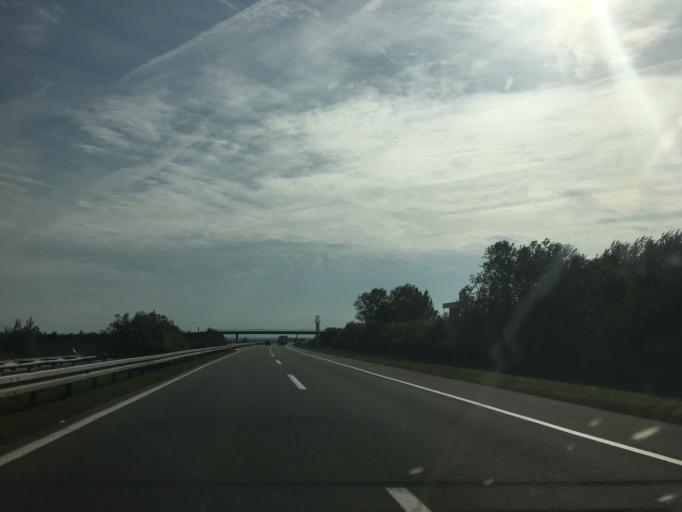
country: RS
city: Novi Banovci
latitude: 44.9191
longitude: 20.3046
